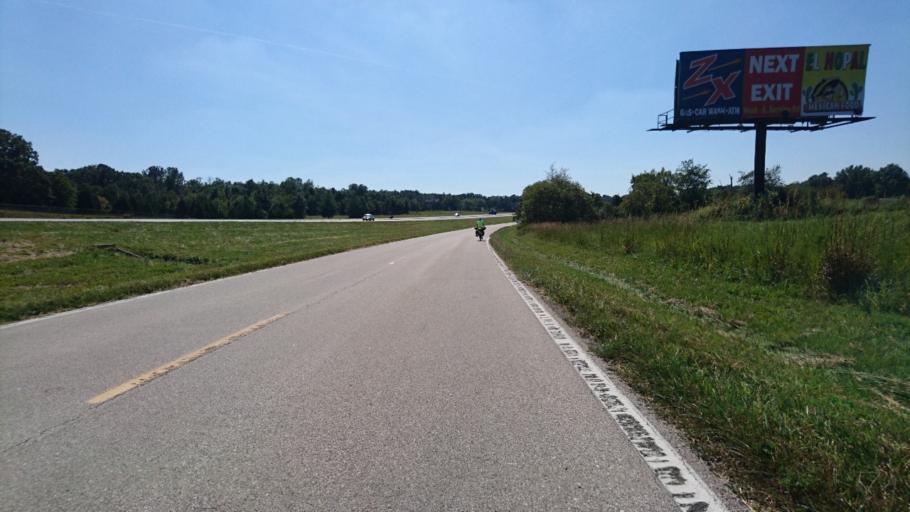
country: US
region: Missouri
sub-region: Franklin County
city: Sullivan
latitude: 38.2685
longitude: -91.1103
